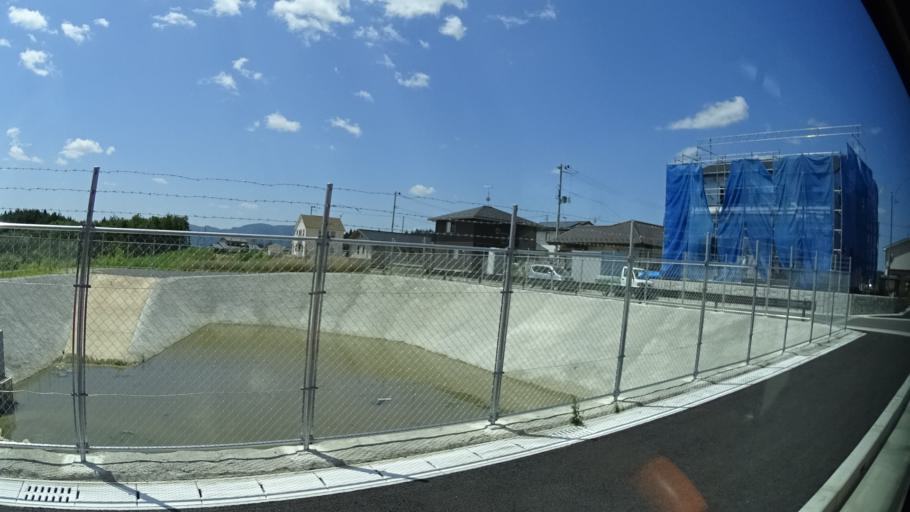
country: JP
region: Iwate
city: Ofunato
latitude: 39.0245
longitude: 141.6433
